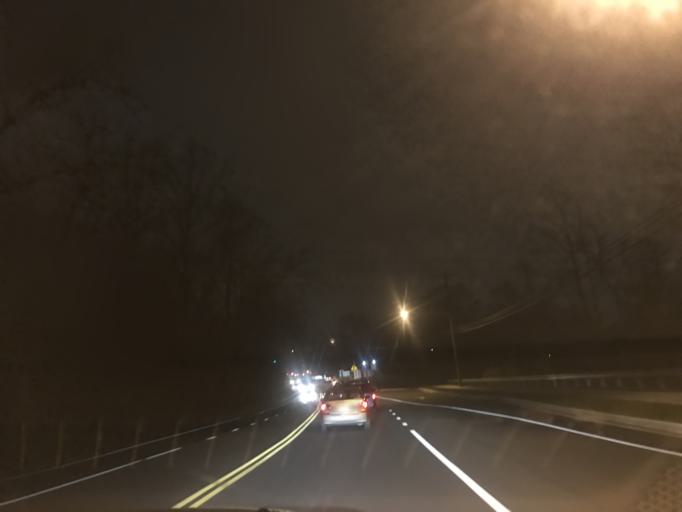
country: US
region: Maryland
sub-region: Prince George's County
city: Temple Hills
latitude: 38.8057
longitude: -76.9612
